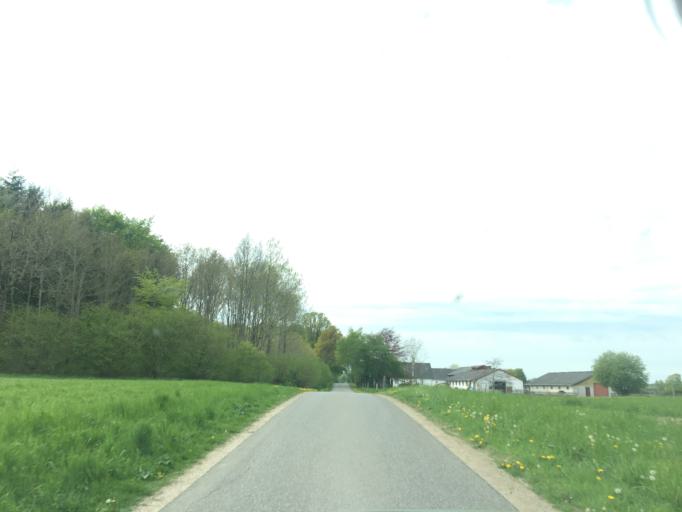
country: DK
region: Zealand
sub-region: Lejre Kommune
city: Osted
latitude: 55.5555
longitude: 11.9447
